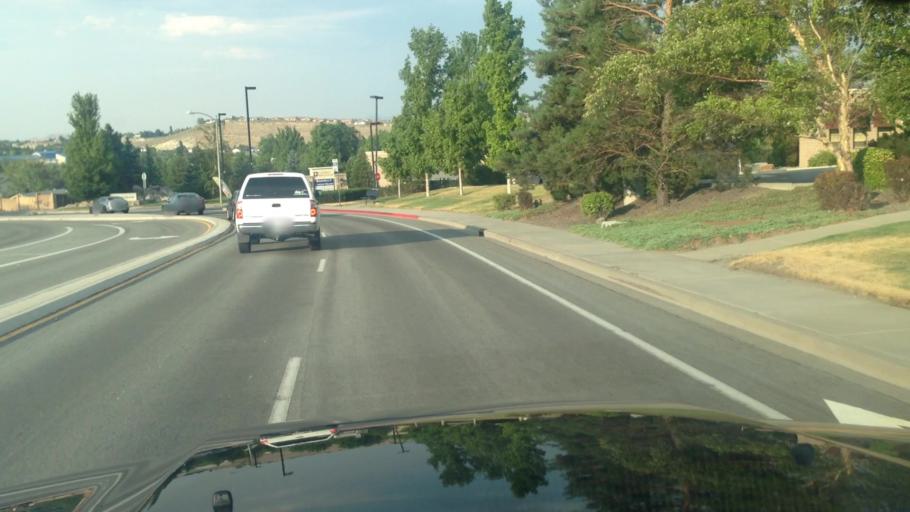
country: US
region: Nevada
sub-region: Washoe County
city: Mogul
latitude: 39.5181
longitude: -119.8858
